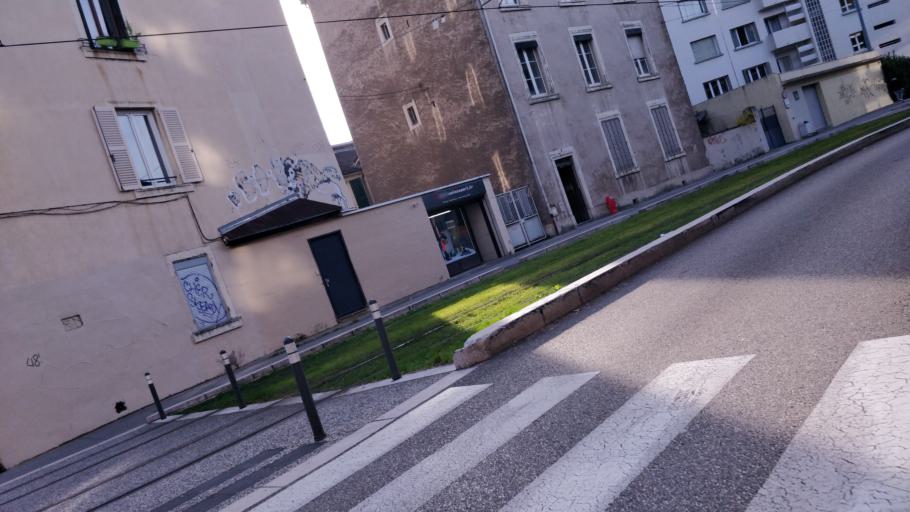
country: FR
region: Rhone-Alpes
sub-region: Departement de l'Isere
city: La Tronche
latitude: 45.1864
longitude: 5.7323
